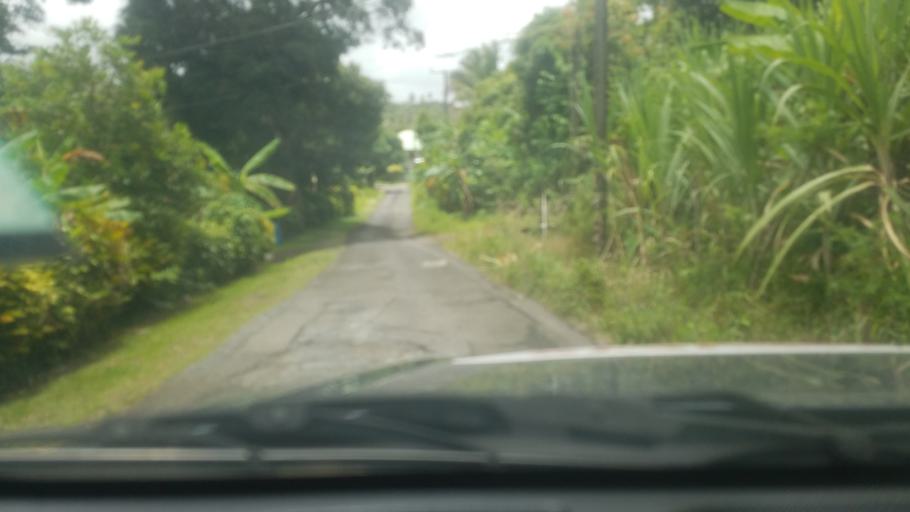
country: LC
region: Laborie Quarter
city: Laborie
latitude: 13.7744
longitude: -61.0009
